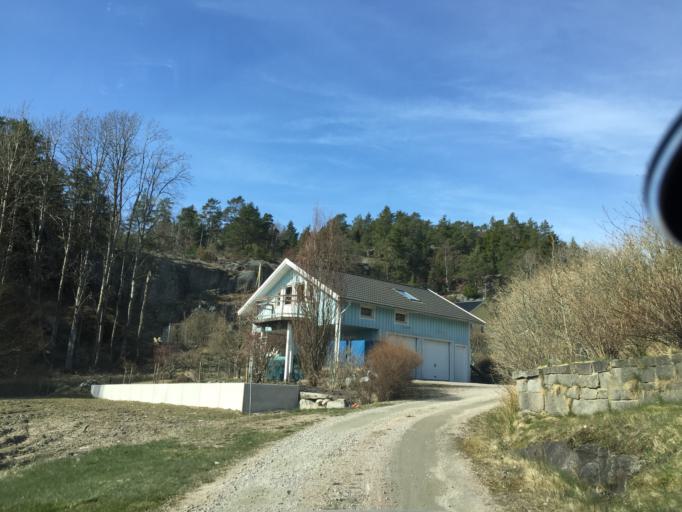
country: SE
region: Vaestra Goetaland
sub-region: Orust
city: Henan
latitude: 58.3432
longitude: 11.7294
